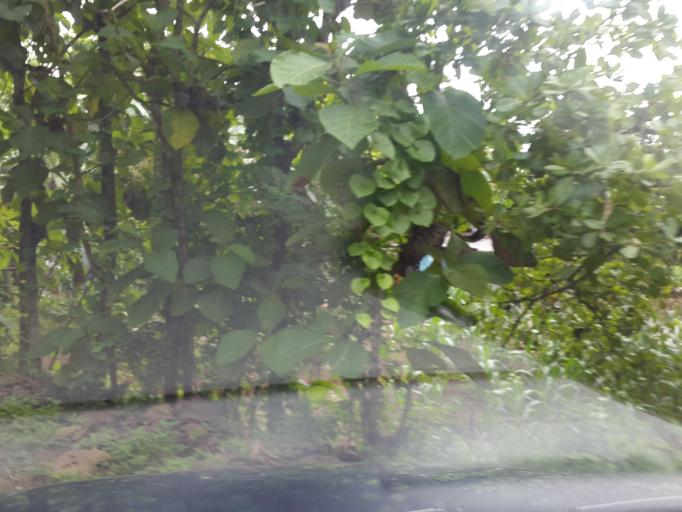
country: ID
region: Daerah Istimewa Yogyakarta
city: Wonosari
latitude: -7.9255
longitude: 110.6809
